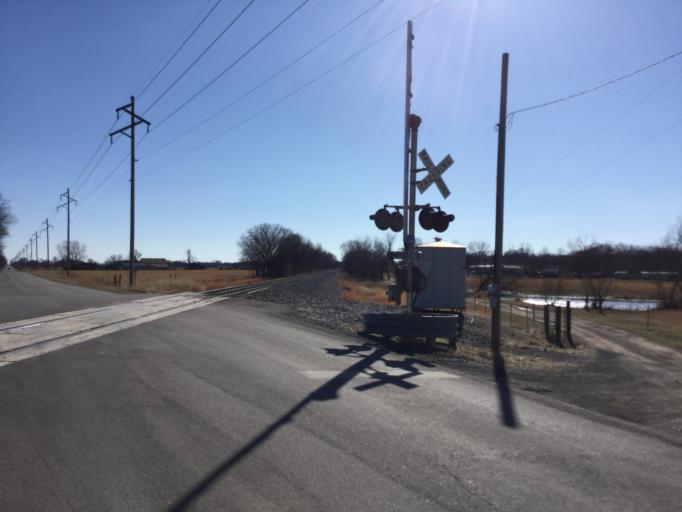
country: US
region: Kansas
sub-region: Crawford County
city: Arma
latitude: 37.5087
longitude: -94.6303
